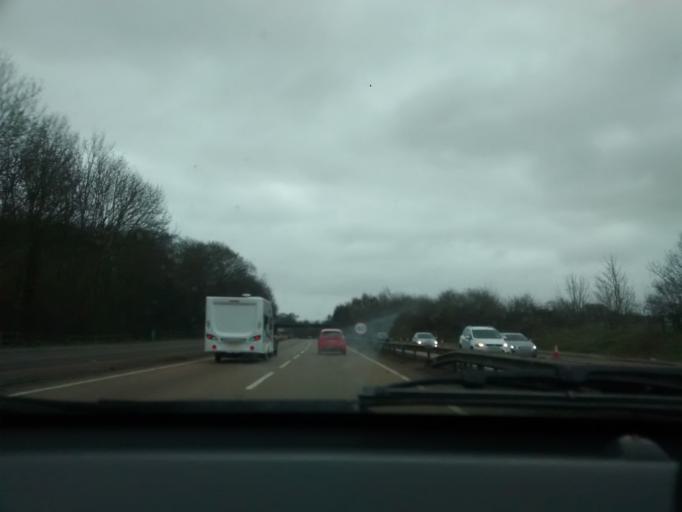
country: GB
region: England
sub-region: Suffolk
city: Ipswich
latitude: 52.0287
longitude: 1.1226
